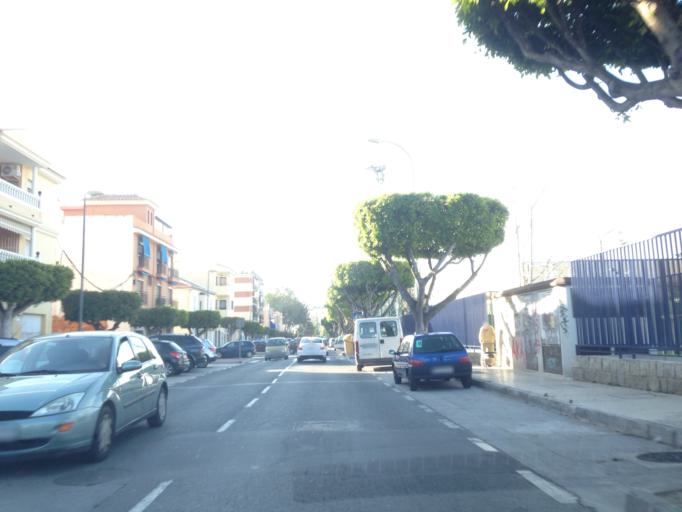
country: ES
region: Andalusia
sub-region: Provincia de Malaga
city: Malaga
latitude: 36.7521
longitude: -4.4236
